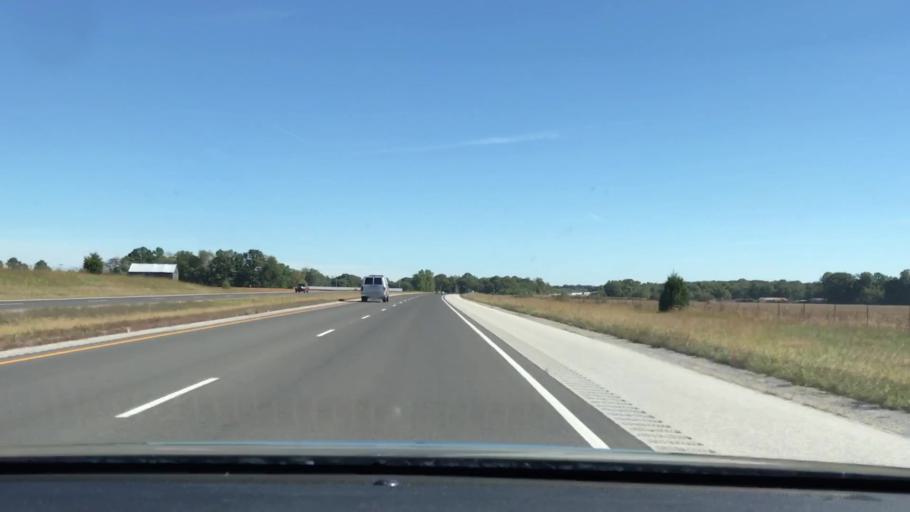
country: US
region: Kentucky
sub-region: Logan County
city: Russellville
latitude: 36.8303
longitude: -86.9766
